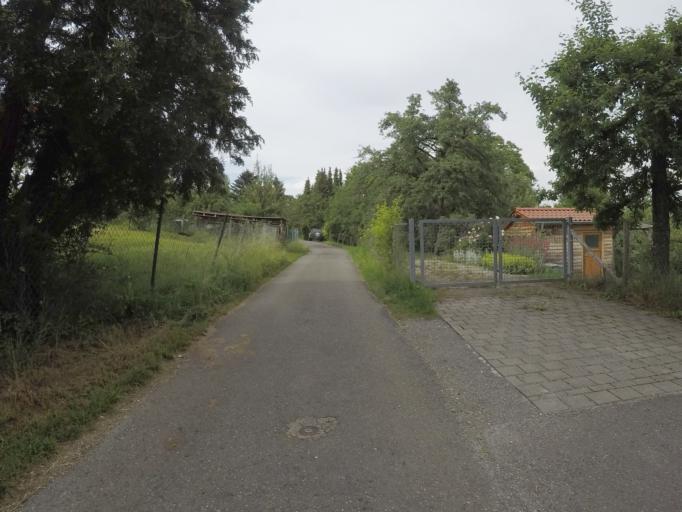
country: DE
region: Baden-Wuerttemberg
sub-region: Tuebingen Region
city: Pfullingen
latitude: 48.4693
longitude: 9.2164
